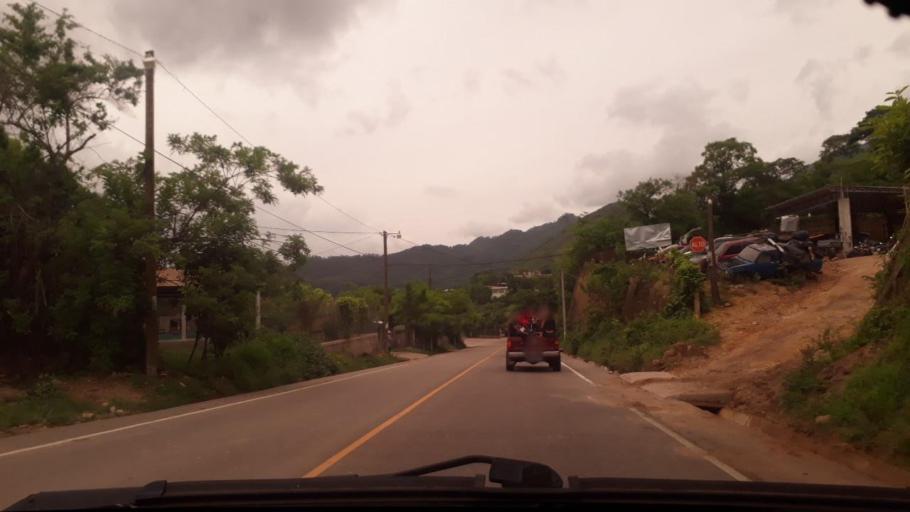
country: GT
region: Chiquimula
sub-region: Municipio de Camotan
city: Camotan
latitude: 14.8192
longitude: -89.3687
